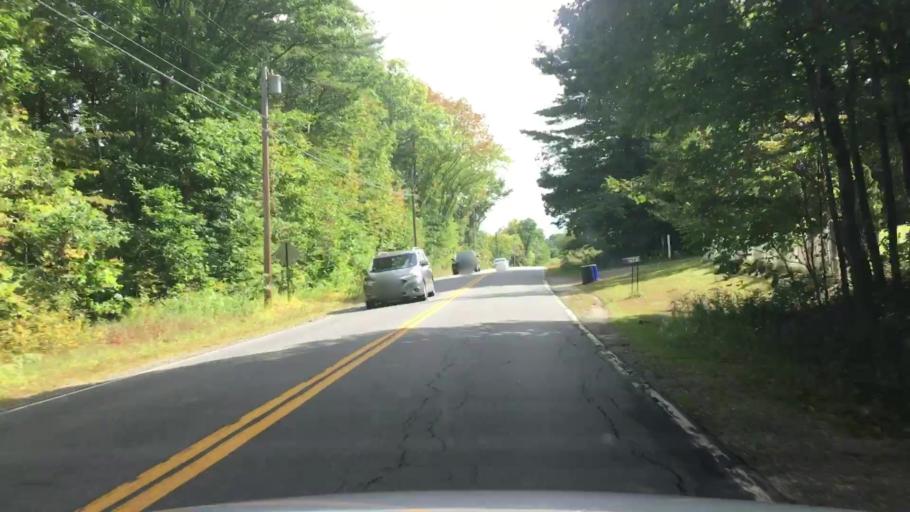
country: US
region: Maine
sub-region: Androscoggin County
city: Lisbon
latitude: 44.0273
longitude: -70.1824
